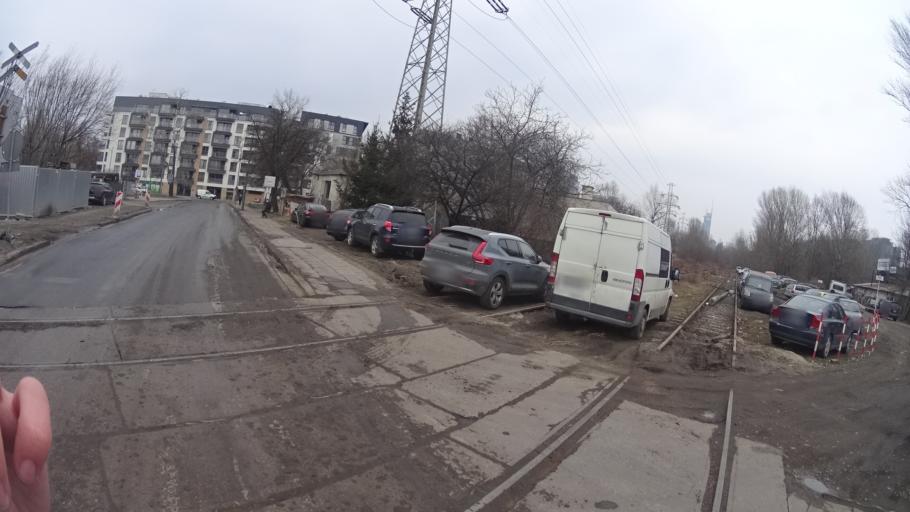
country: PL
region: Masovian Voivodeship
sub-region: Warszawa
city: Ochota
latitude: 52.2225
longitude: 20.9692
